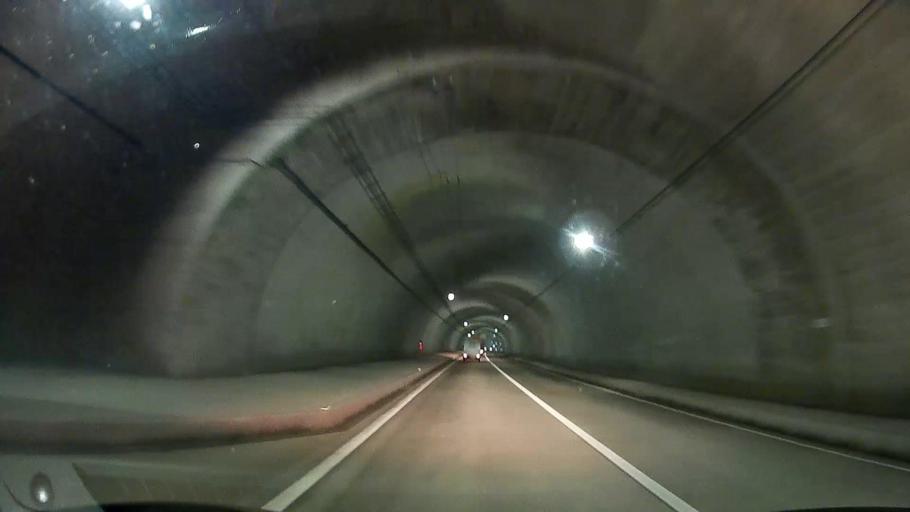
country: JP
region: Gunma
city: Nakanojomachi
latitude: 36.5327
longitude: 138.7123
